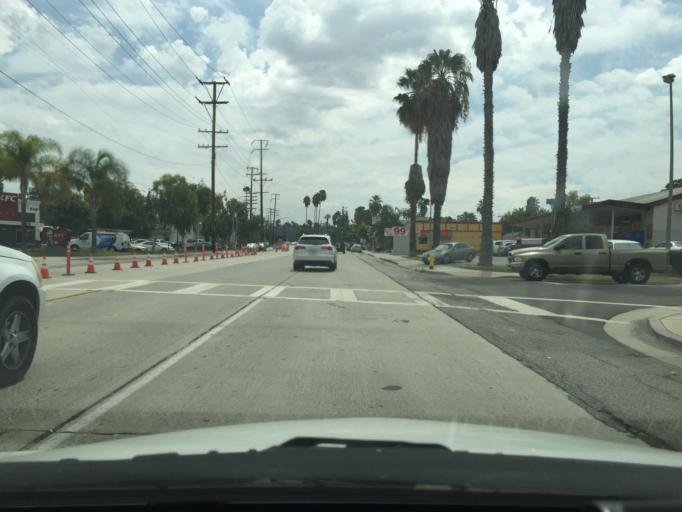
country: US
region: California
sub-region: San Bernardino County
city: Redlands
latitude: 34.0548
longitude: -117.1752
